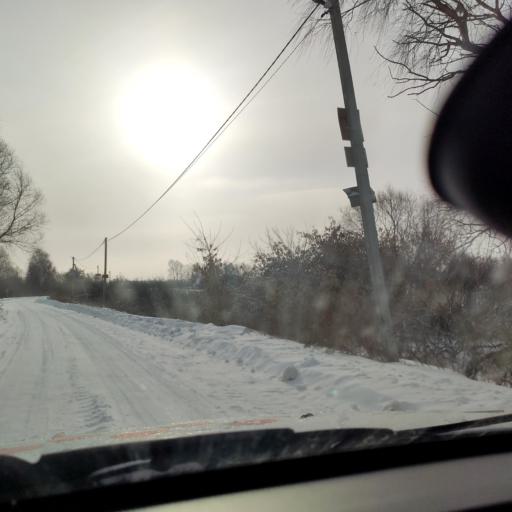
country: RU
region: Bashkortostan
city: Mikhaylovka
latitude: 54.8690
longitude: 55.7511
